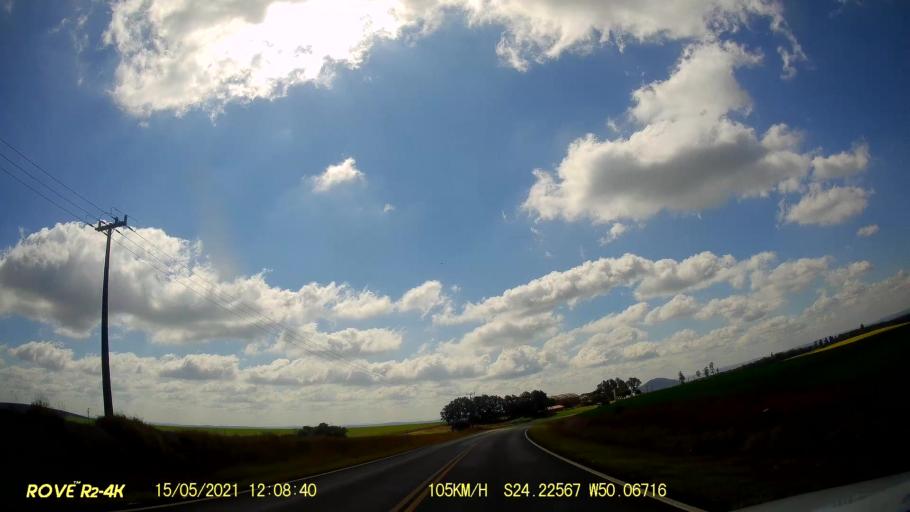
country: BR
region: Parana
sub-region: Pirai Do Sul
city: Pirai do Sul
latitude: -24.2260
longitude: -50.0669
